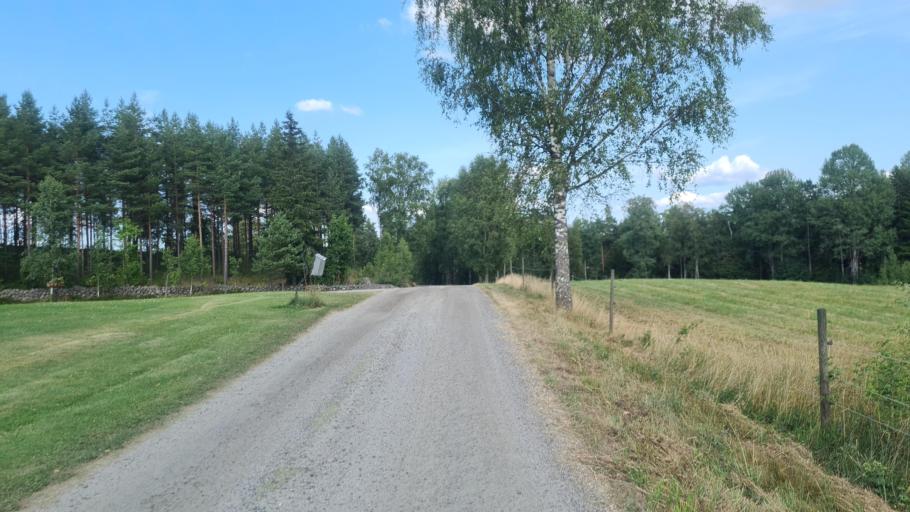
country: SE
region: Kronoberg
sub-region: Ljungby Kommun
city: Ljungby
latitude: 56.7188
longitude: 13.8794
